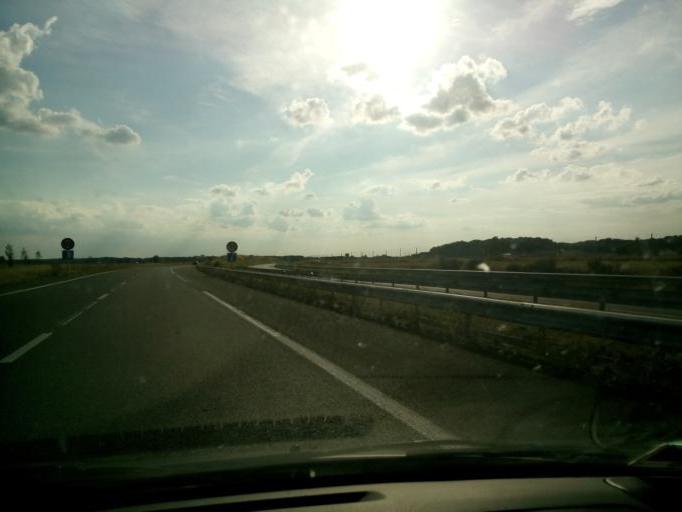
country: FR
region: Centre
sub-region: Departement d'Indre-et-Loire
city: Savonnieres
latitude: 47.3066
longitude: 0.5675
